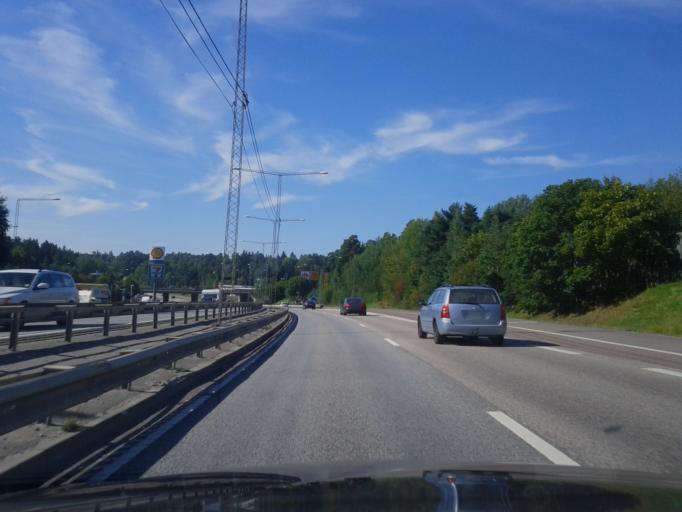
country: SE
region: Stockholm
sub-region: Taby Kommun
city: Taby
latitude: 59.4363
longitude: 18.0729
